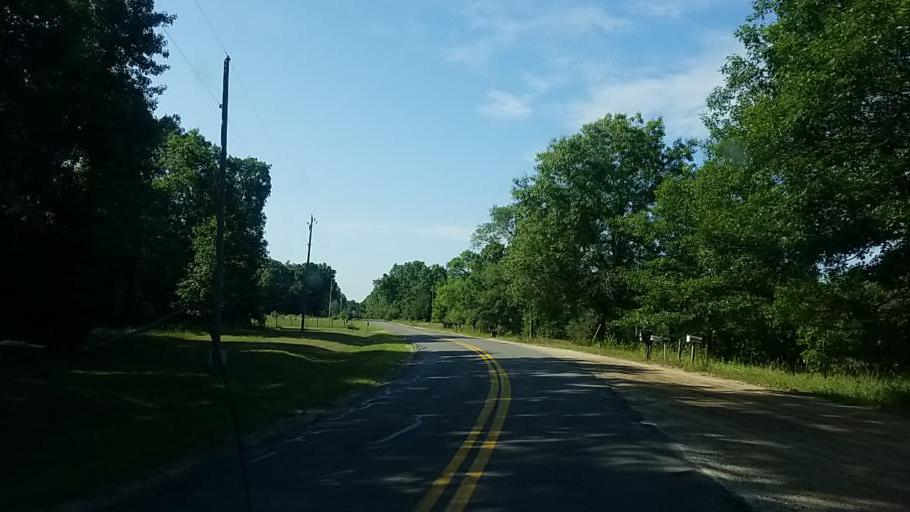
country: US
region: Michigan
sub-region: Muskegon County
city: Twin Lake
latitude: 43.4680
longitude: -86.1932
